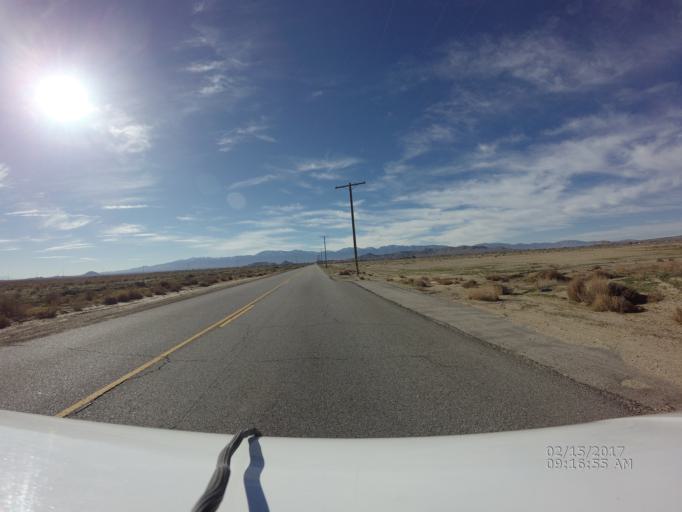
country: US
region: California
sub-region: Los Angeles County
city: Lake Los Angeles
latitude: 34.6526
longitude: -117.8274
